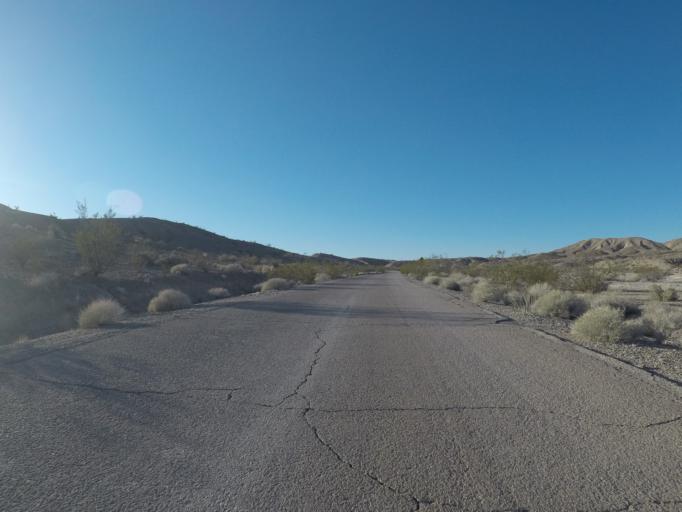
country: US
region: Nevada
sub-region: Clark County
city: Moapa Valley
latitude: 36.3885
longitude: -114.4175
